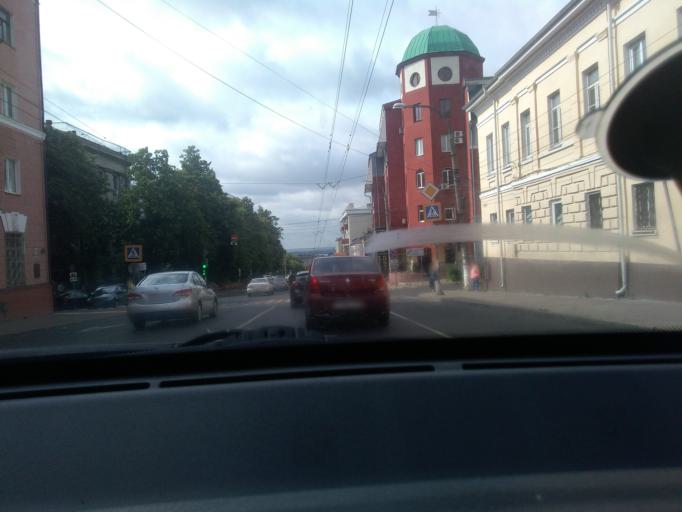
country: RU
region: Kursk
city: Kursk
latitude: 51.7318
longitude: 36.1903
